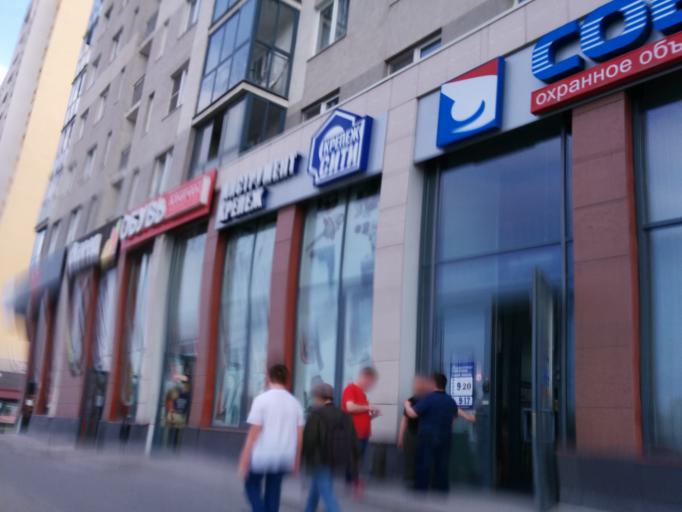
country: RU
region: Sverdlovsk
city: Shirokaya Rechka
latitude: 56.7921
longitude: 60.5229
